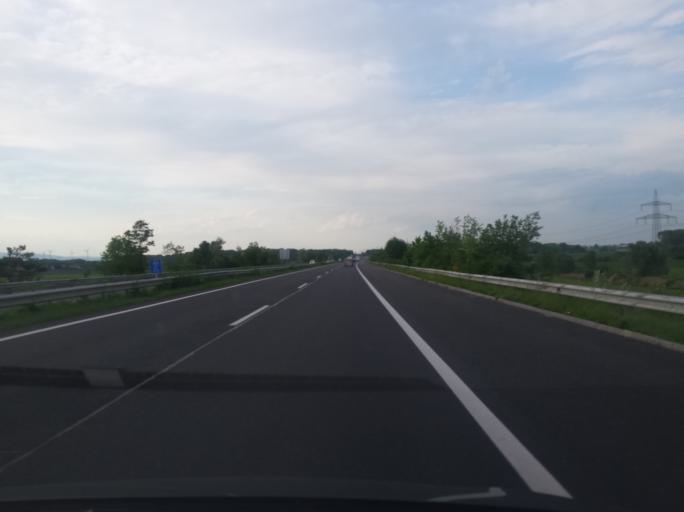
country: AT
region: Burgenland
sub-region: Eisenstadt-Umgebung
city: Hornstein
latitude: 47.8801
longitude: 16.4157
